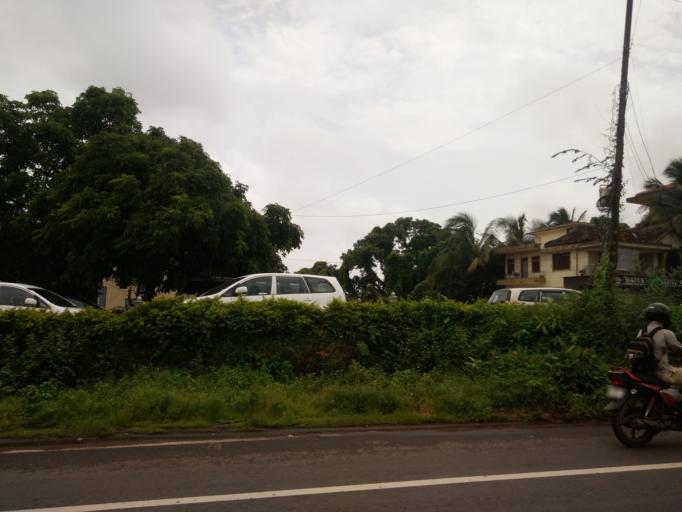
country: IN
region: Goa
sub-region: North Goa
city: Panaji
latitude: 15.5172
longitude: 73.8326
